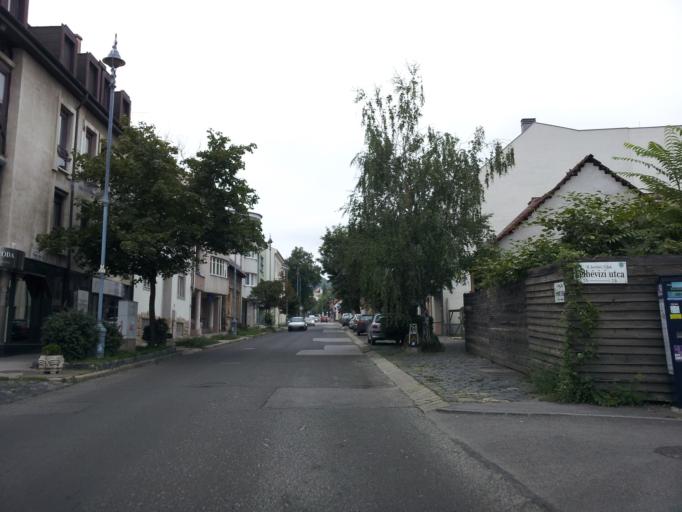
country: HU
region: Budapest
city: Budapest II. keruelet
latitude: 47.5266
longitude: 19.0349
